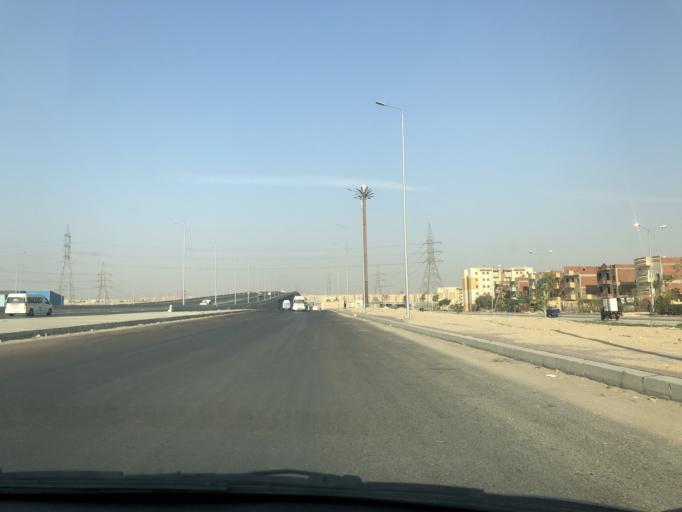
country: EG
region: Al Jizah
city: Madinat Sittah Uktubar
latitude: 29.9083
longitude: 30.9256
